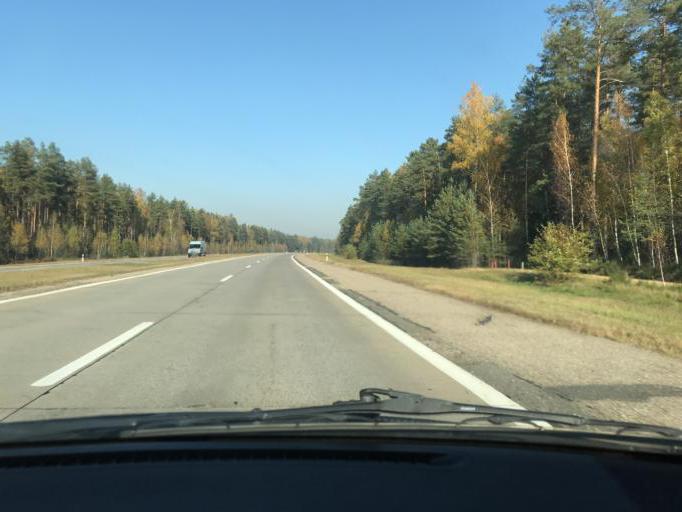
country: BY
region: Minsk
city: Uzda
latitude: 53.4013
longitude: 27.4810
